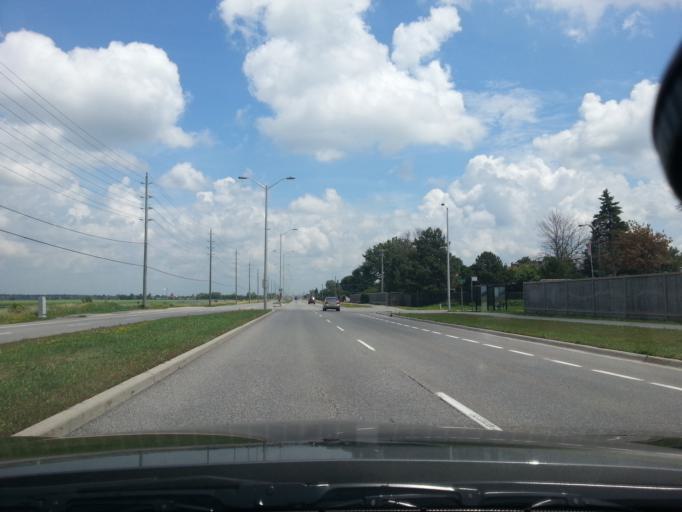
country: CA
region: Ontario
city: Bells Corners
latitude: 45.2914
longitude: -75.7494
